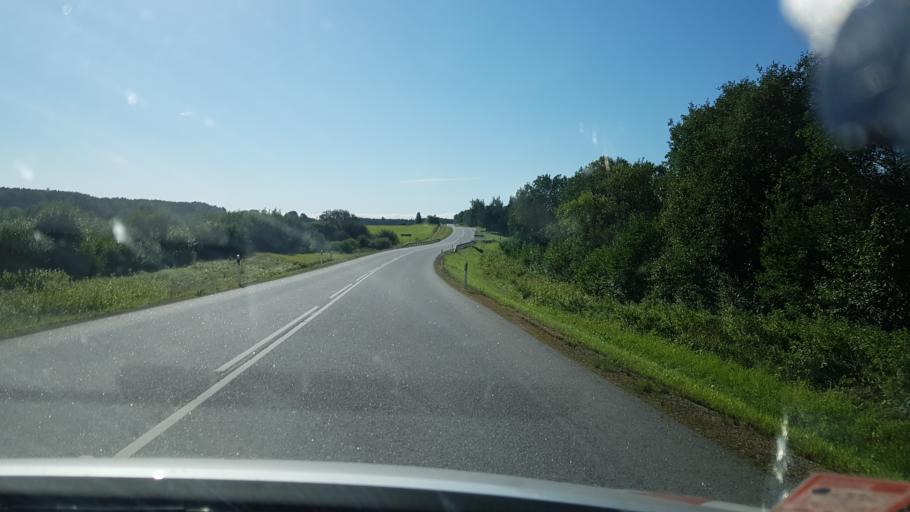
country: EE
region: Valgamaa
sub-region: Valga linn
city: Valga
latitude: 57.7279
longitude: 26.1780
